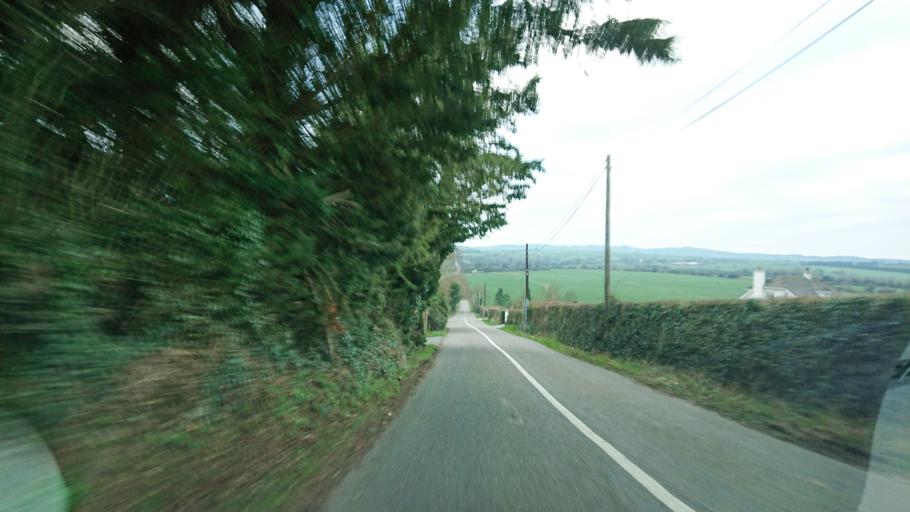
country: IE
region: Munster
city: Carrick-on-Suir
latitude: 52.3133
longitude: -7.5286
